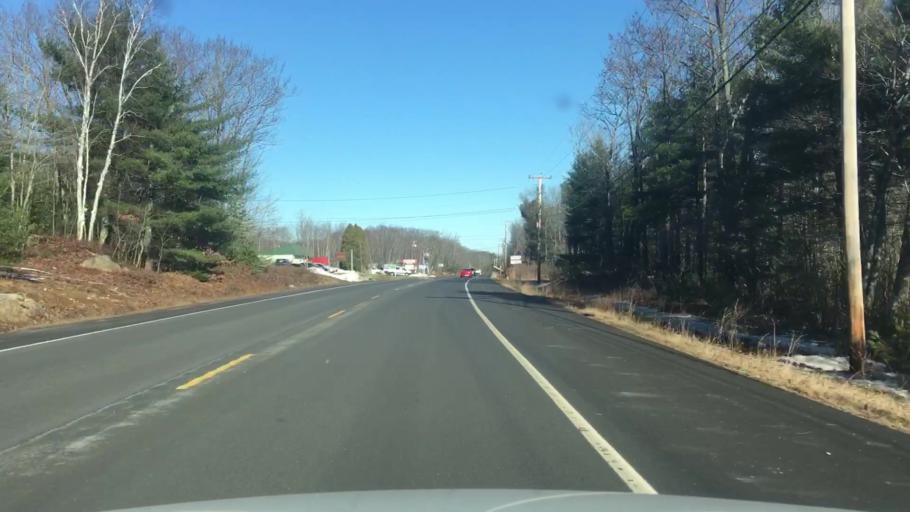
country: US
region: Maine
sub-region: York County
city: Arundel
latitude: 43.4384
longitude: -70.5035
